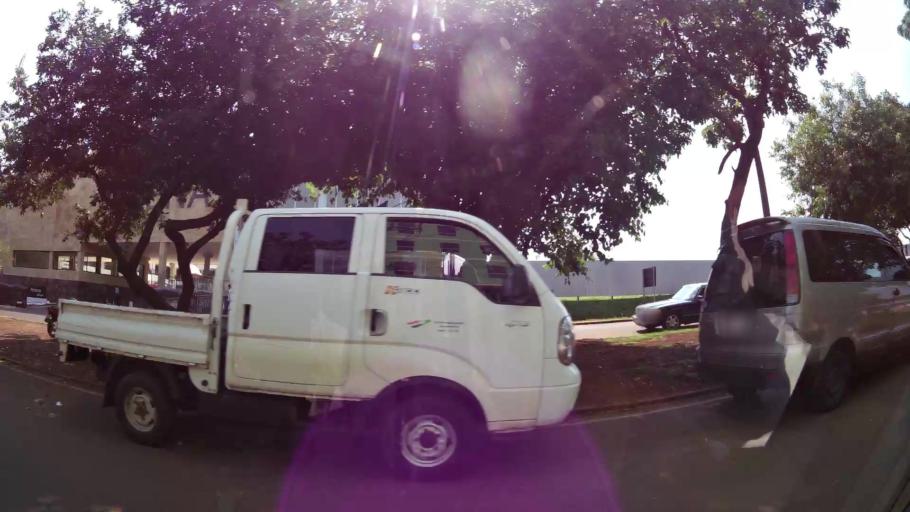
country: PY
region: Alto Parana
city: Ciudad del Este
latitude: -25.5105
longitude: -54.6341
